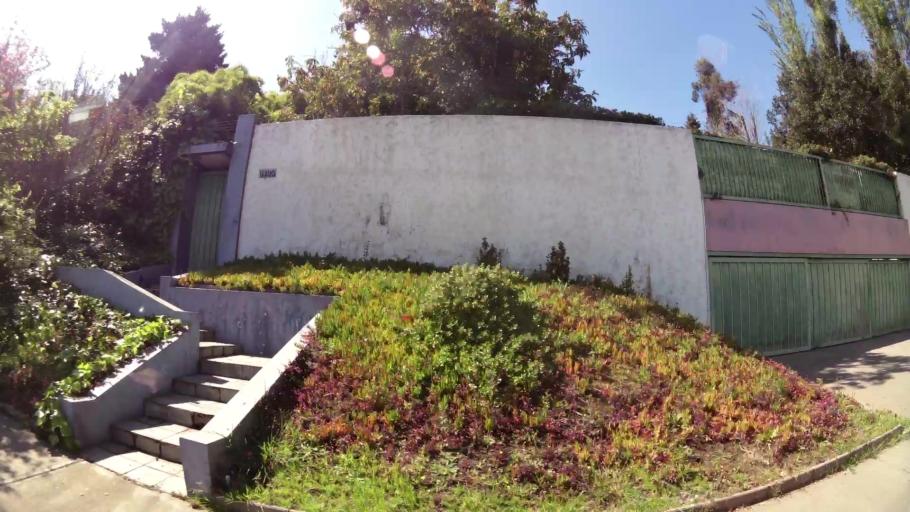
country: CL
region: Santiago Metropolitan
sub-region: Provincia de Santiago
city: Villa Presidente Frei, Nunoa, Santiago, Chile
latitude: -33.4570
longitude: -70.5210
